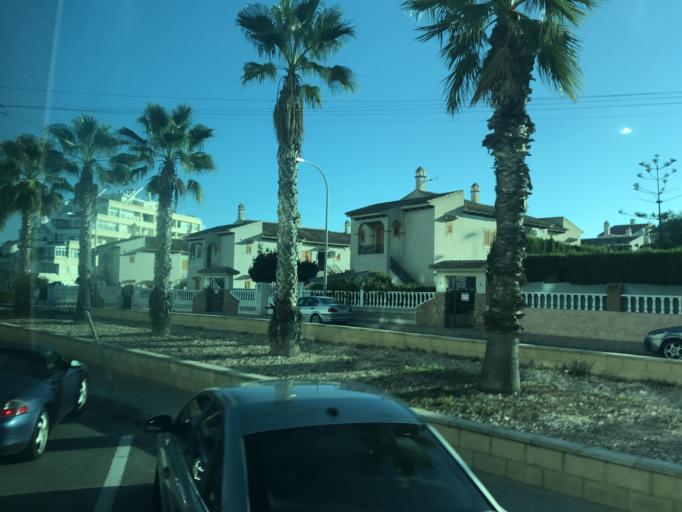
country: ES
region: Valencia
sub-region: Provincia de Alicante
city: Torrevieja
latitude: 38.0041
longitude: -0.6556
